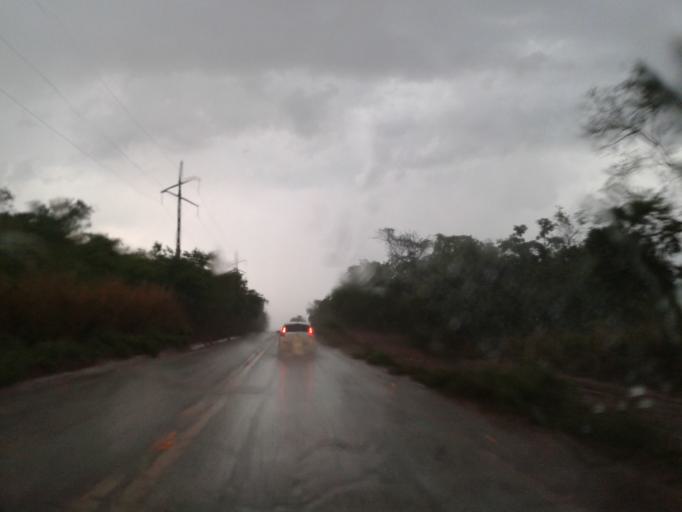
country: BR
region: Goias
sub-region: Quirinopolis
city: Quirinopolis
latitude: -18.5285
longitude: -50.4436
